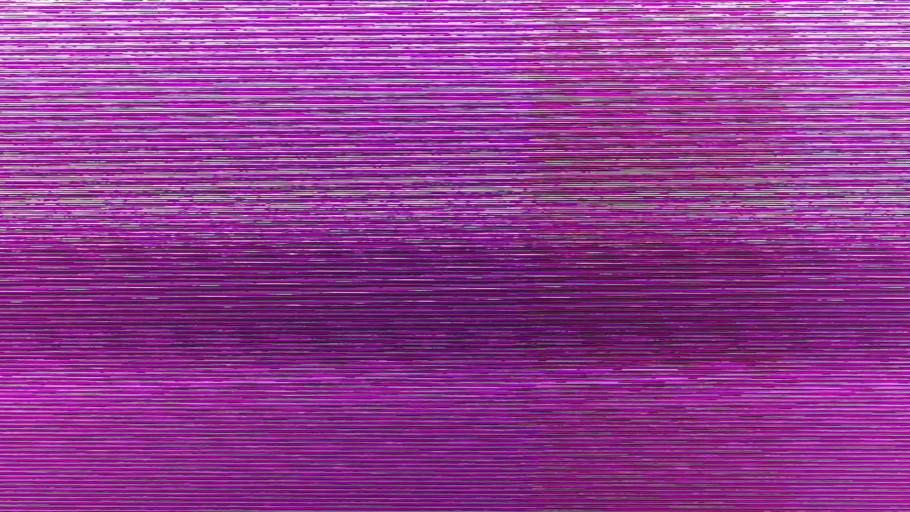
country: US
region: Michigan
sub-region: Genesee County
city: Linden
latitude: 42.8195
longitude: -83.7825
